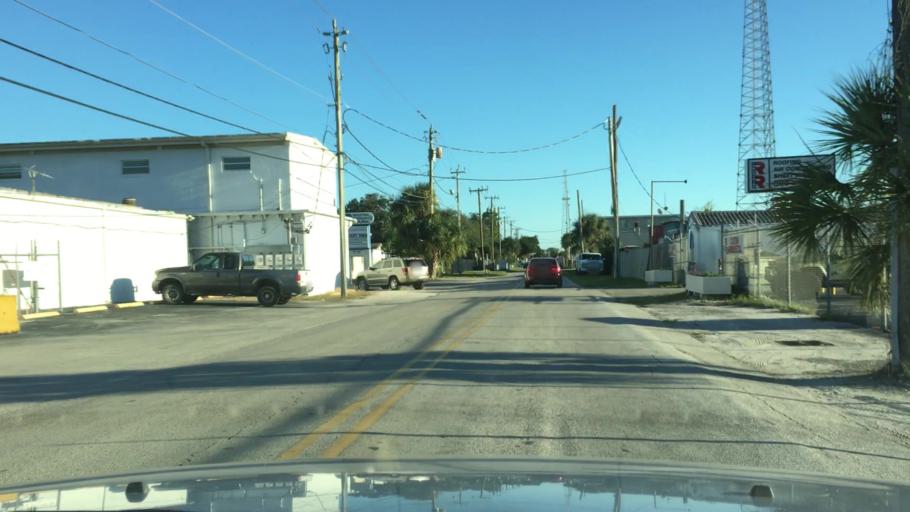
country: US
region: Florida
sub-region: Volusia County
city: Holly Hill
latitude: 29.2342
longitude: -81.0375
